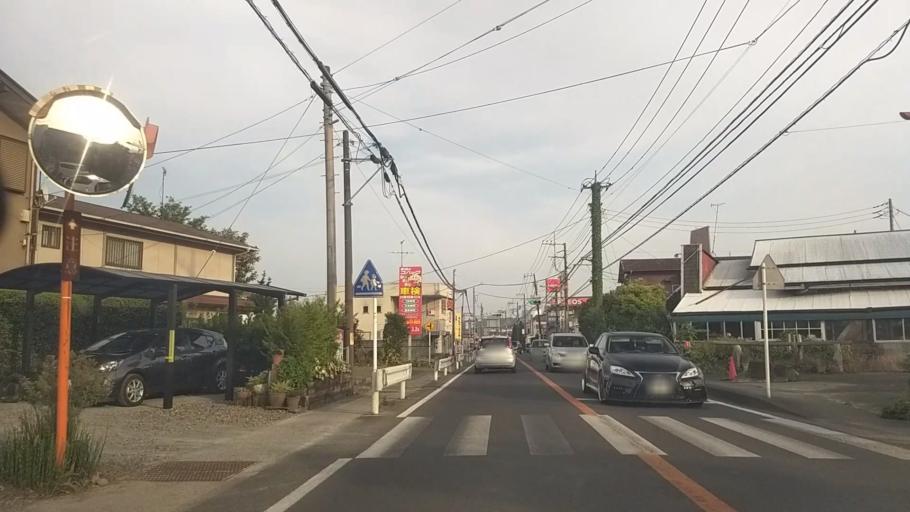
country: JP
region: Kanagawa
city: Odawara
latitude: 35.2945
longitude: 139.1317
